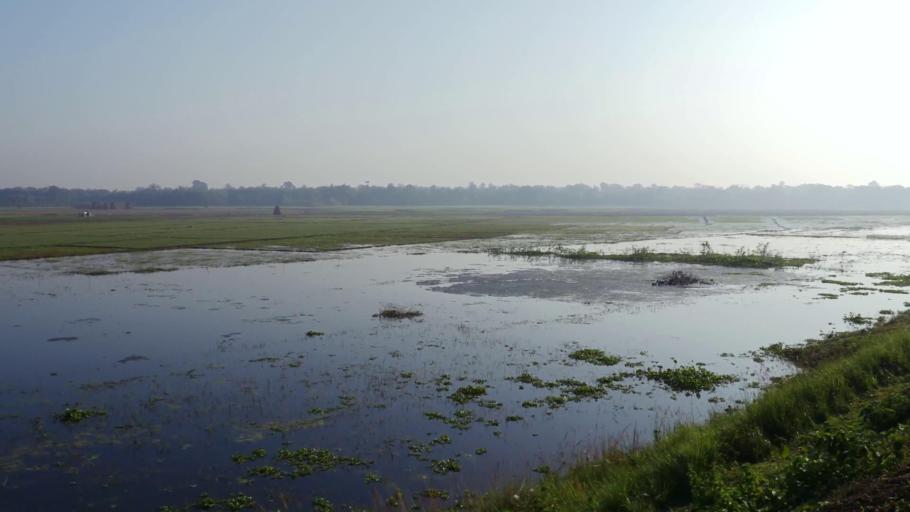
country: BD
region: Dhaka
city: Jamalpur
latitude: 24.9188
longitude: 89.9439
